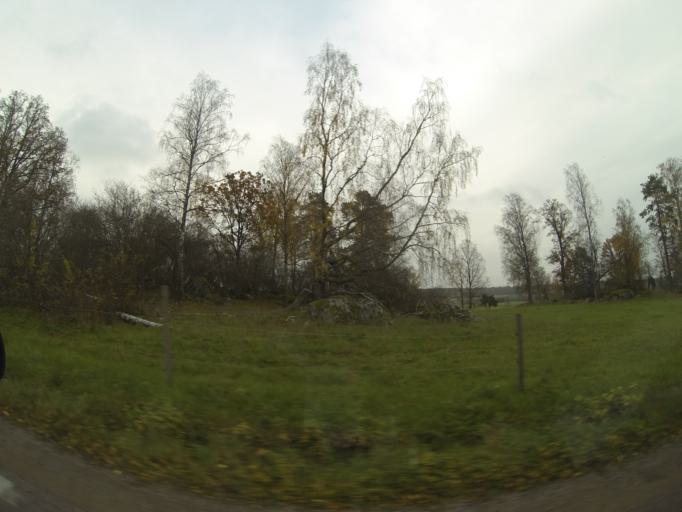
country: SE
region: Vaestmanland
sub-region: Vasteras
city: Skultuna
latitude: 59.6688
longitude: 16.4599
